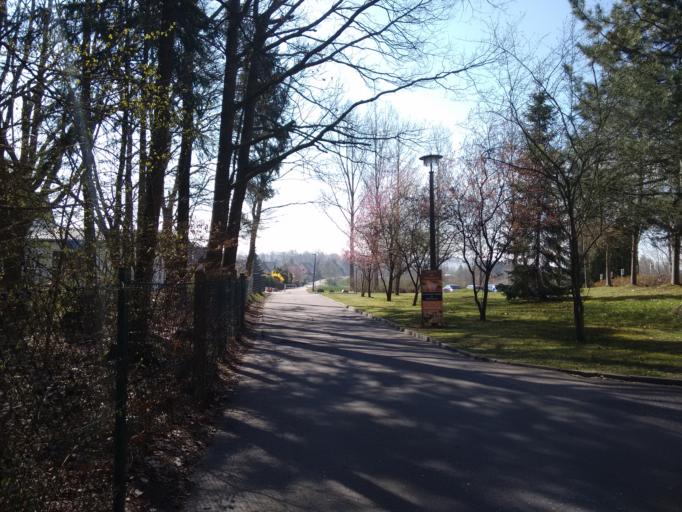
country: DE
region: Saxony
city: Limbach-Oberfrohna
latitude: 50.8534
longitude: 12.7690
